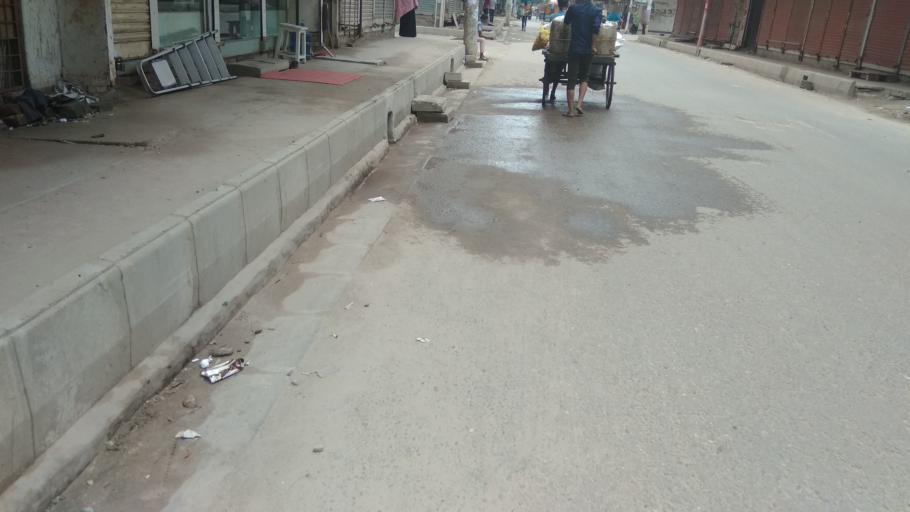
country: BD
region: Dhaka
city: Azimpur
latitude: 23.8113
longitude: 90.3699
